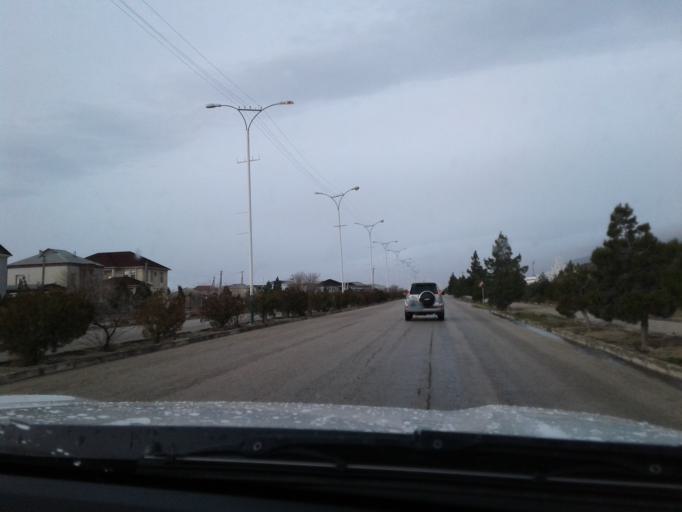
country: TM
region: Balkan
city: Balkanabat
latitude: 39.5357
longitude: 54.3519
